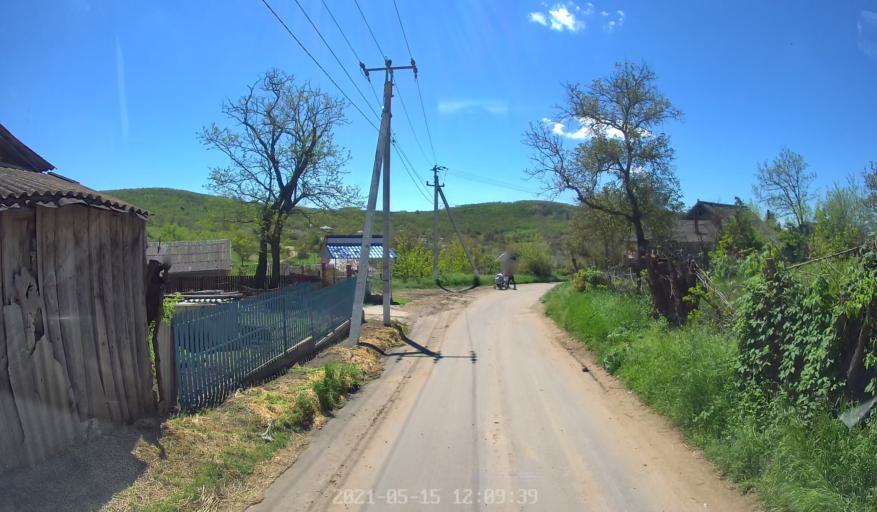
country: MD
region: Hincesti
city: Hincesti
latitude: 46.7987
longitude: 28.5417
